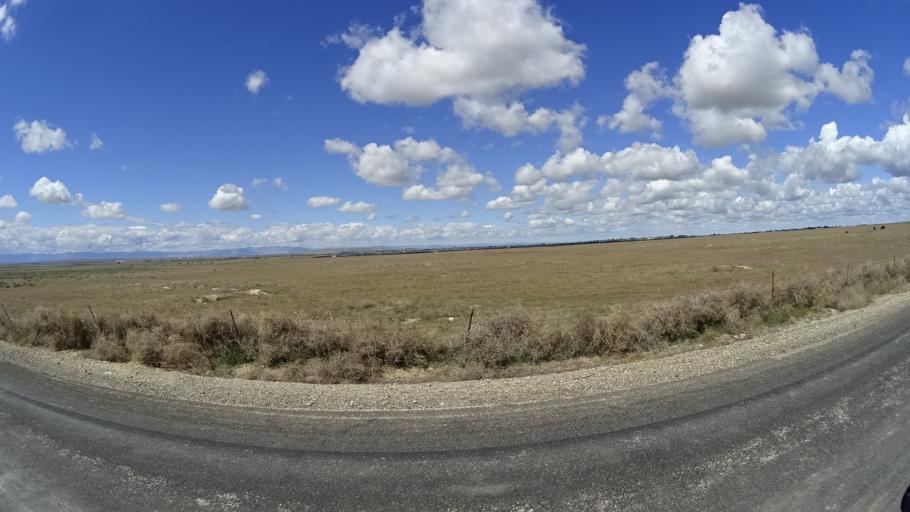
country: US
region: Idaho
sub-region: Ada County
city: Kuna
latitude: 43.4669
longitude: -116.2744
